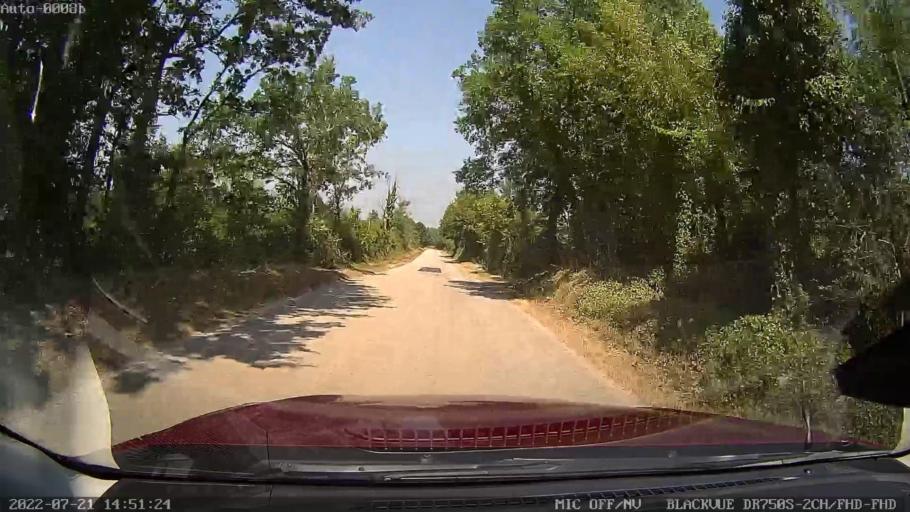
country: HR
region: Istarska
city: Pazin
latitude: 45.1684
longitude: 13.9222
